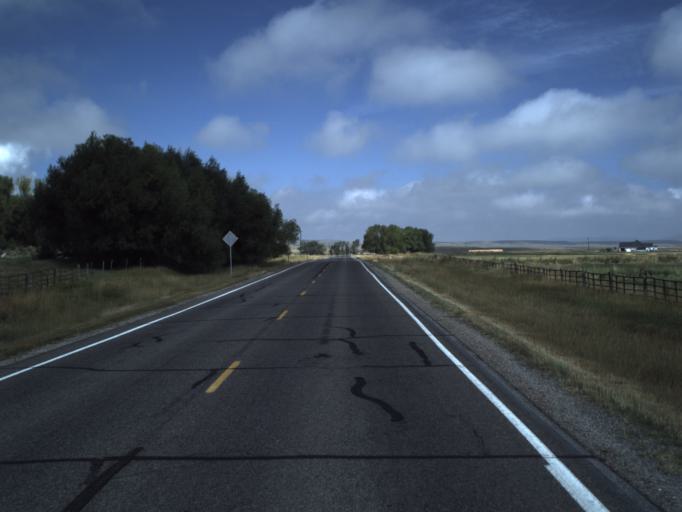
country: US
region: Utah
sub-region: Rich County
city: Randolph
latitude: 41.7089
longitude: -111.1594
